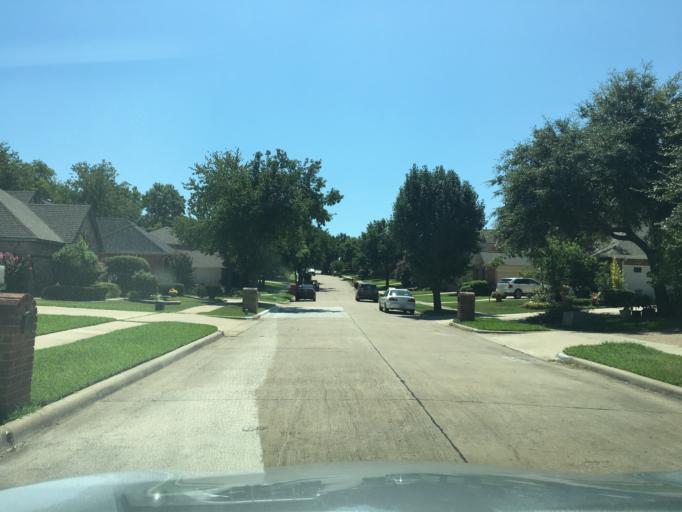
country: US
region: Texas
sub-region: Dallas County
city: Sachse
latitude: 32.9641
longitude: -96.6250
